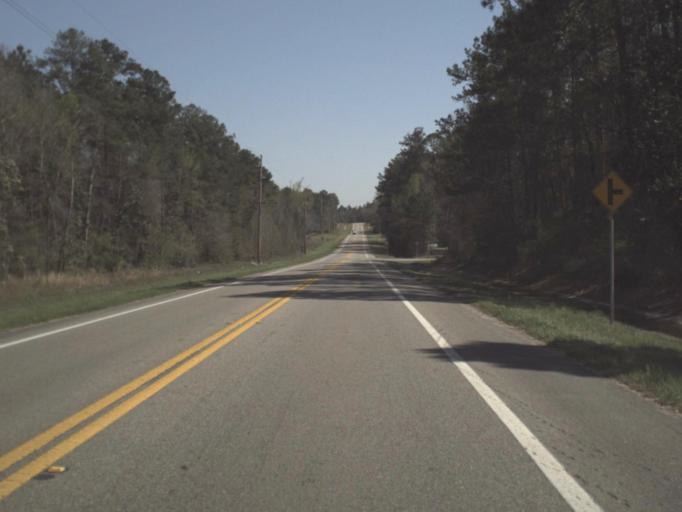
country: US
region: Florida
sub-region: Liberty County
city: Bristol
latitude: 30.3985
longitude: -84.8114
